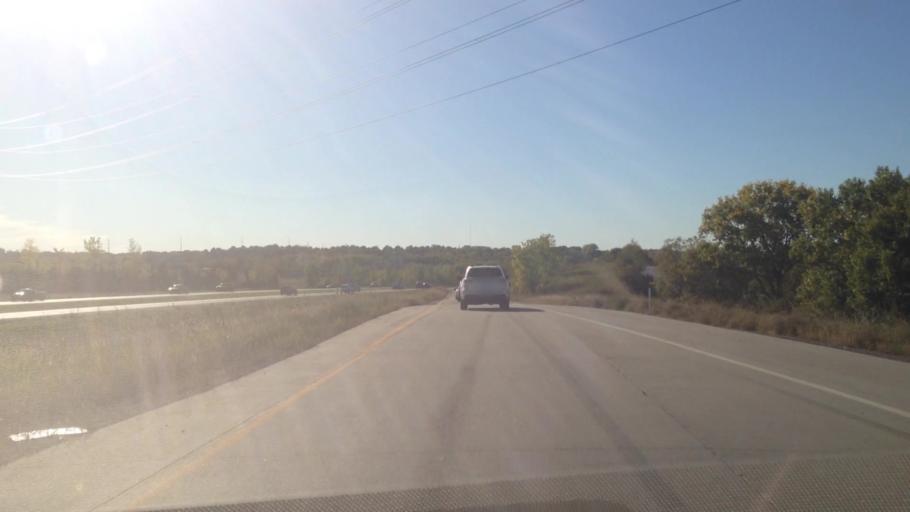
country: US
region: Kansas
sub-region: Johnson County
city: Olathe
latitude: 38.9422
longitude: -94.7982
